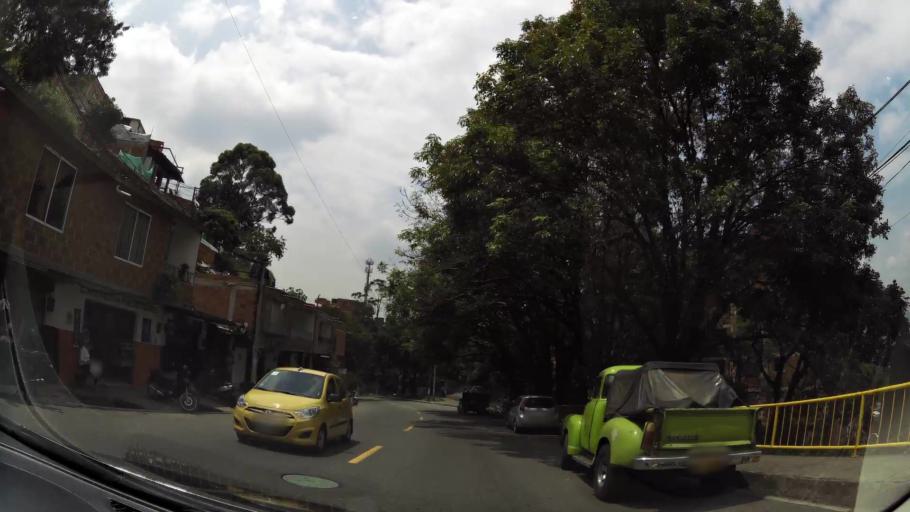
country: CO
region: Antioquia
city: Medellin
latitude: 6.2620
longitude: -75.5551
